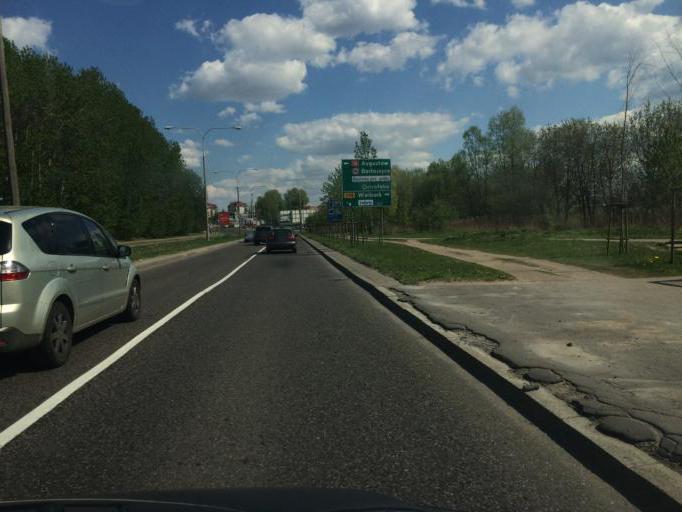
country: PL
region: Warmian-Masurian Voivodeship
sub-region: Olsztyn
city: Kortowo
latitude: 53.7654
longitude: 20.4768
